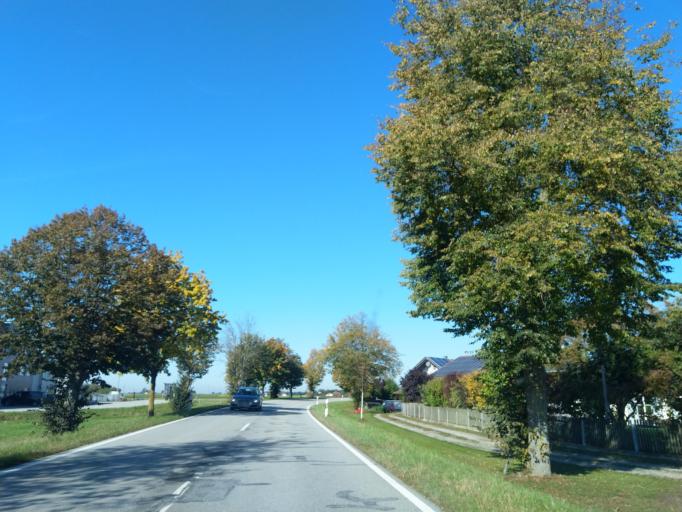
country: DE
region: Bavaria
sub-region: Lower Bavaria
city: Stephansposching
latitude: 48.8023
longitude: 12.8027
